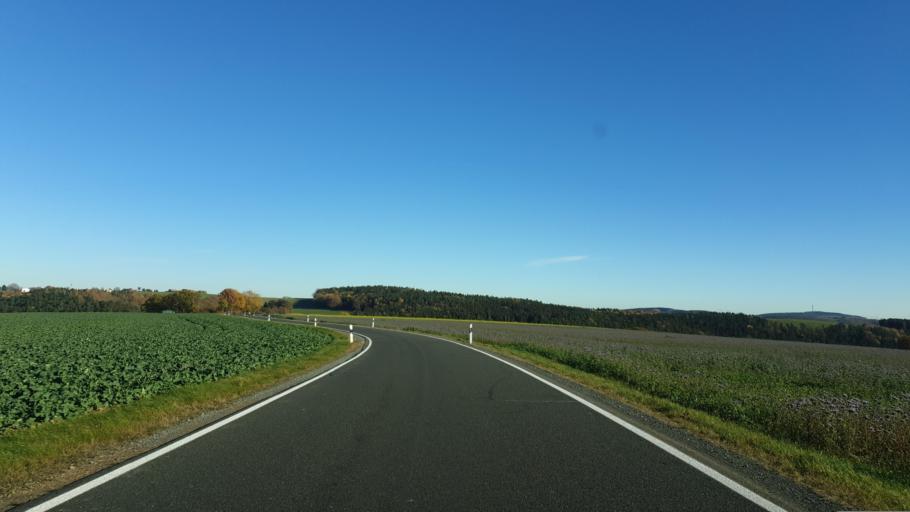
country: DE
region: Saxony
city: Elsterberg
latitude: 50.6275
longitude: 12.1317
